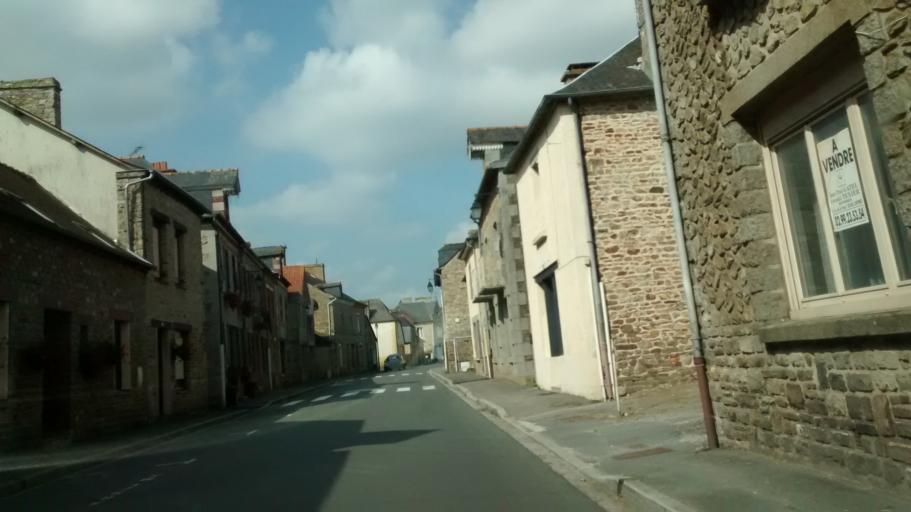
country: FR
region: Brittany
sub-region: Departement d'Ille-et-Vilaine
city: Livre-sur-Changeon
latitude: 48.2192
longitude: -1.3432
